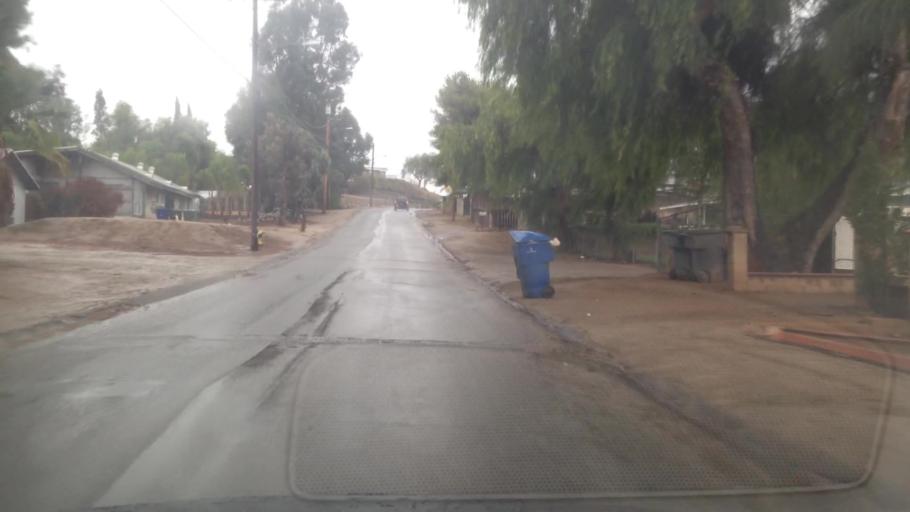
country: US
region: California
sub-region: Riverside County
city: Pedley
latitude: 33.9349
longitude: -117.4870
